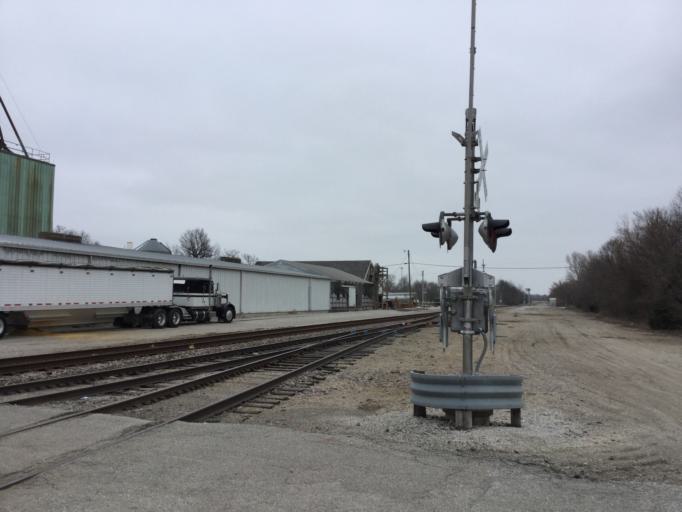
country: US
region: Kansas
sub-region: Cherokee County
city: Baxter Springs
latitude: 37.0262
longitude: -94.7442
